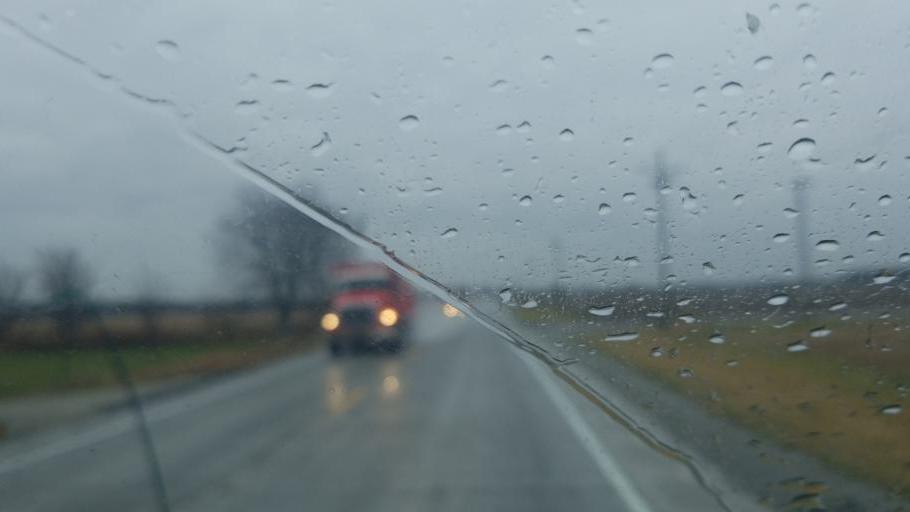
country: US
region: Indiana
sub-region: Shelby County
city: Geneva
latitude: 39.4099
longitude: -85.7508
